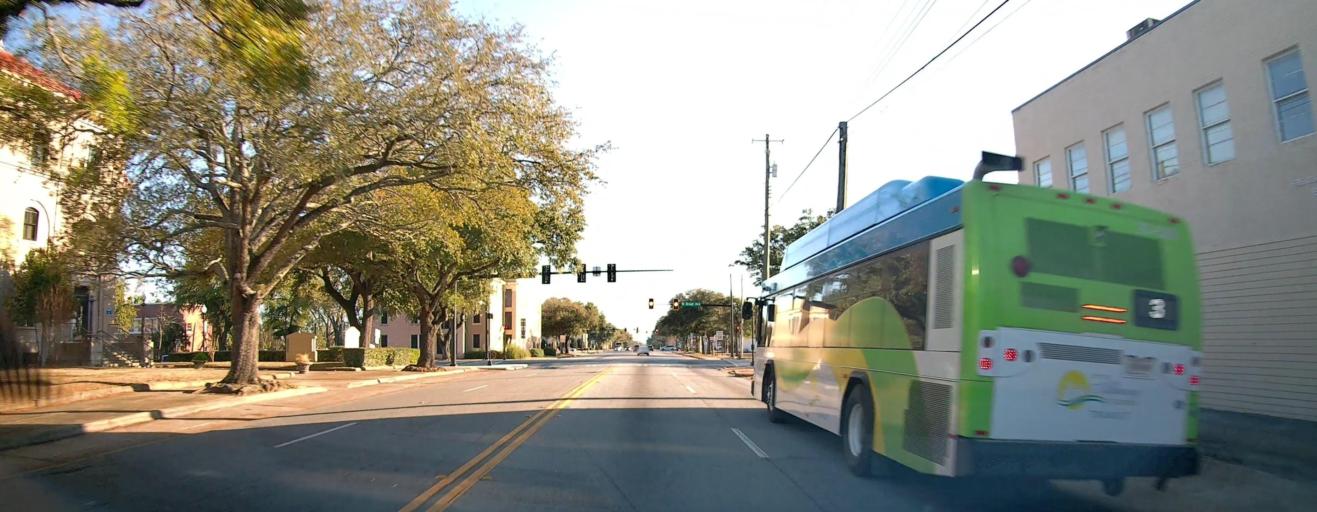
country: US
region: Georgia
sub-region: Dougherty County
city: Albany
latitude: 31.5776
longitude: -84.1560
